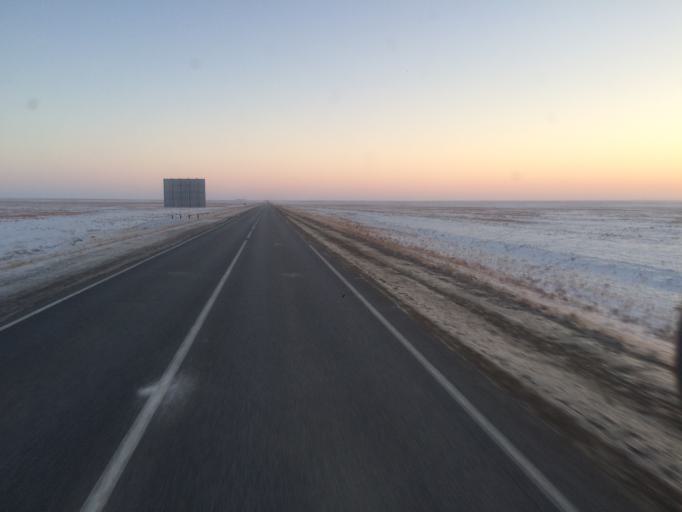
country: KZ
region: Qyzylorda
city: Sekseuil
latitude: 47.4788
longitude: 61.5358
